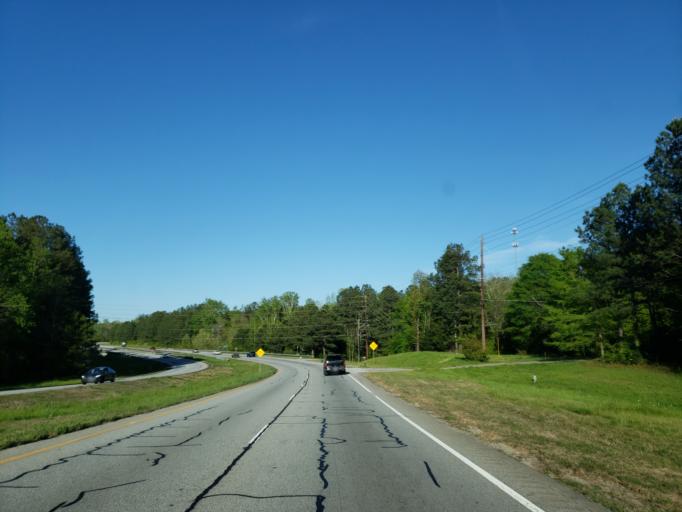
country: US
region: Georgia
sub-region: Paulding County
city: Dallas
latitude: 33.9151
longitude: -84.8807
